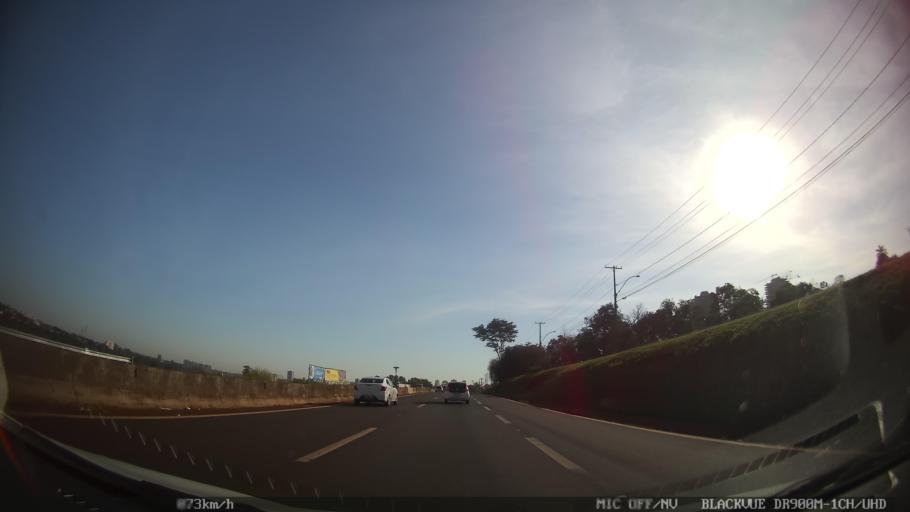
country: BR
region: Sao Paulo
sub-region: Ribeirao Preto
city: Ribeirao Preto
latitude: -21.2435
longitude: -47.8192
